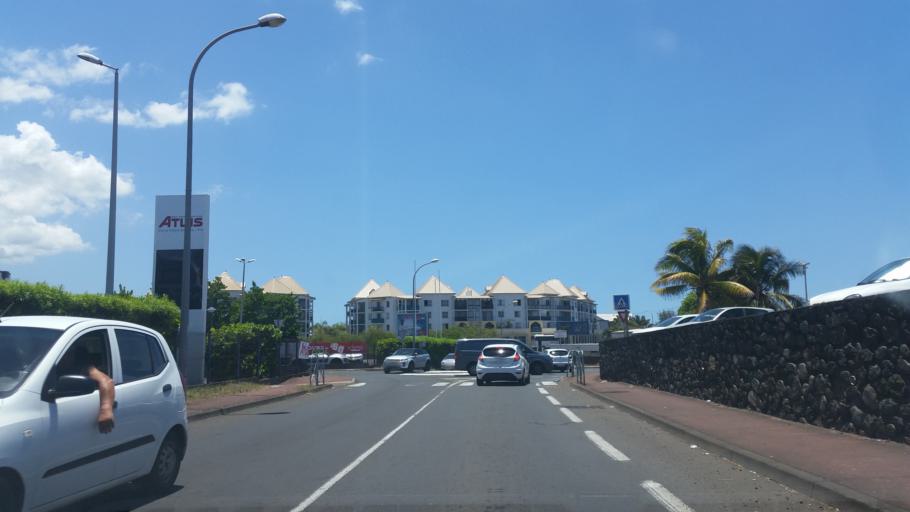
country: RE
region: Reunion
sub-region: Reunion
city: Saint-Pierre
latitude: -21.3359
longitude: 55.4564
